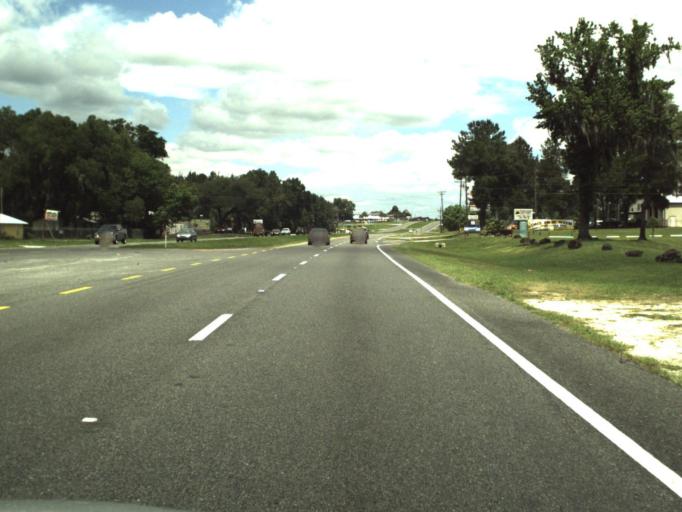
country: US
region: Florida
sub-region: Marion County
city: Ocala
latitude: 29.2382
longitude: -82.1517
